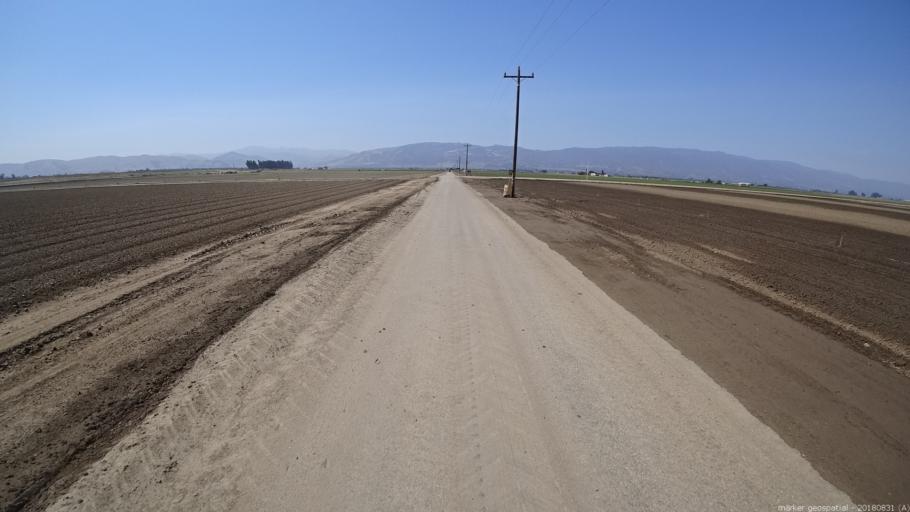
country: US
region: California
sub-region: Monterey County
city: Greenfield
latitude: 36.3565
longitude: -121.2588
